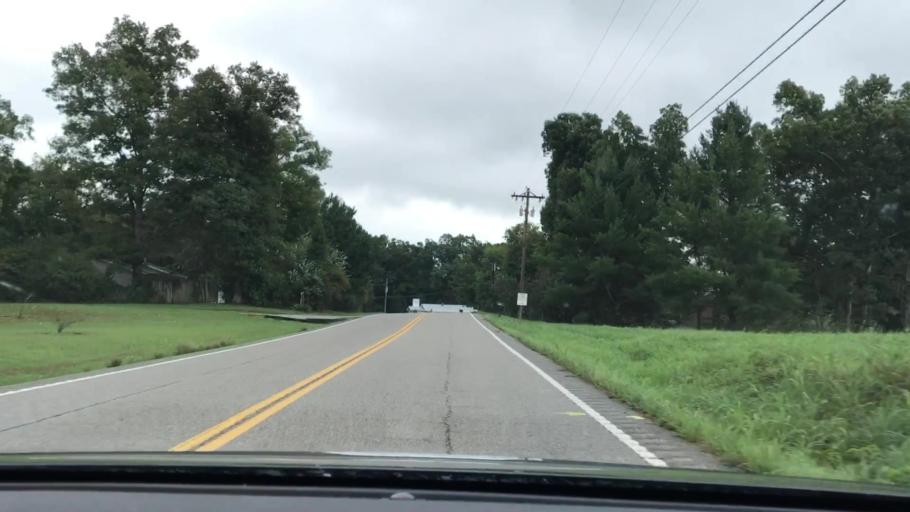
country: US
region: Tennessee
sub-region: Scott County
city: Huntsville
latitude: 36.3474
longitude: -84.6796
